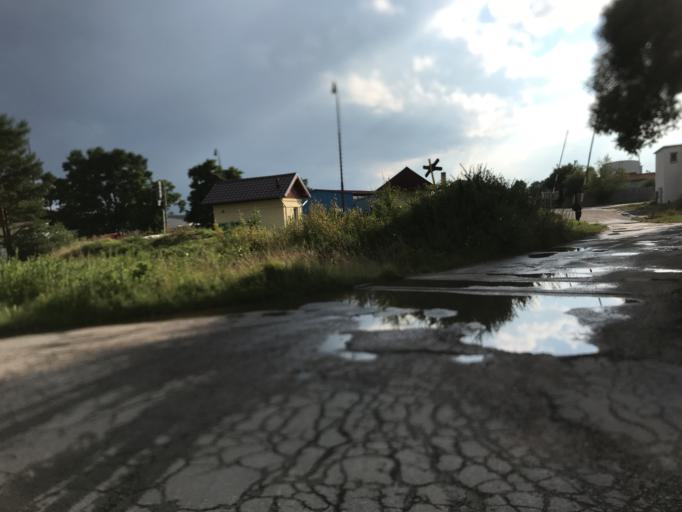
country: CZ
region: Jihocesky
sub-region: Okres Jindrichuv Hradec
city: Trebon
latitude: 49.0179
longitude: 14.7601
